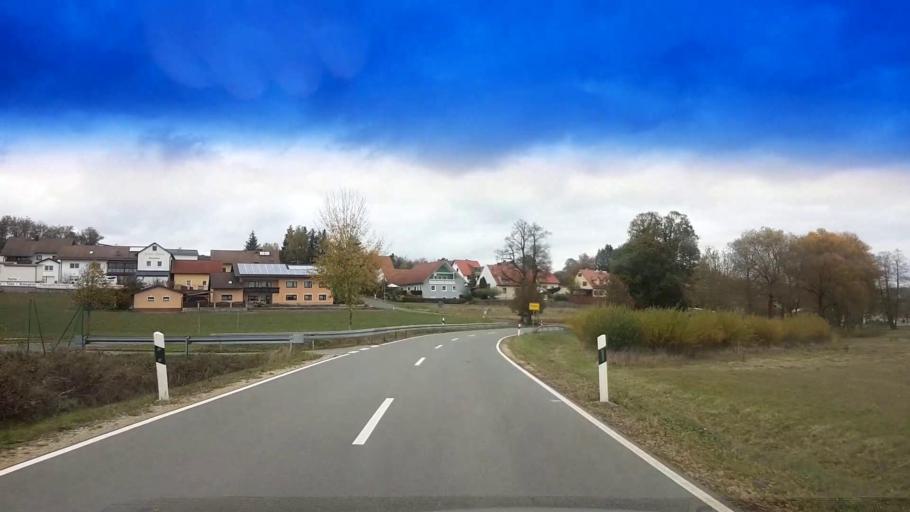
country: DE
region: Bavaria
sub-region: Upper Franconia
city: Konigsfeld
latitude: 49.9437
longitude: 11.1589
